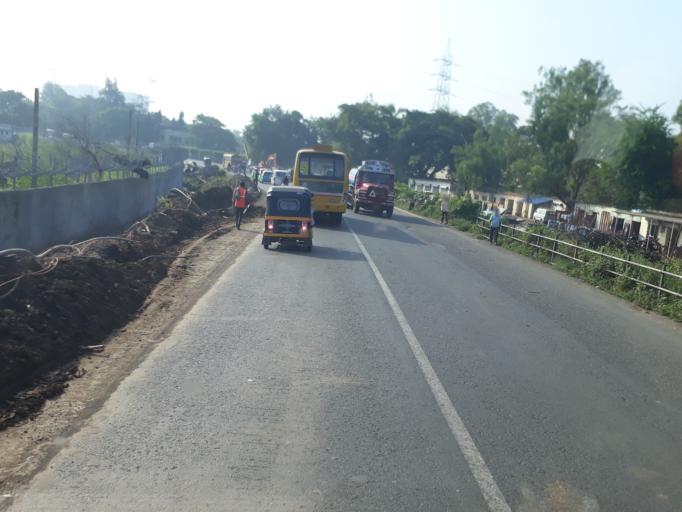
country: IN
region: Maharashtra
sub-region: Raigarh
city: Kalundri
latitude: 18.9768
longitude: 73.1170
